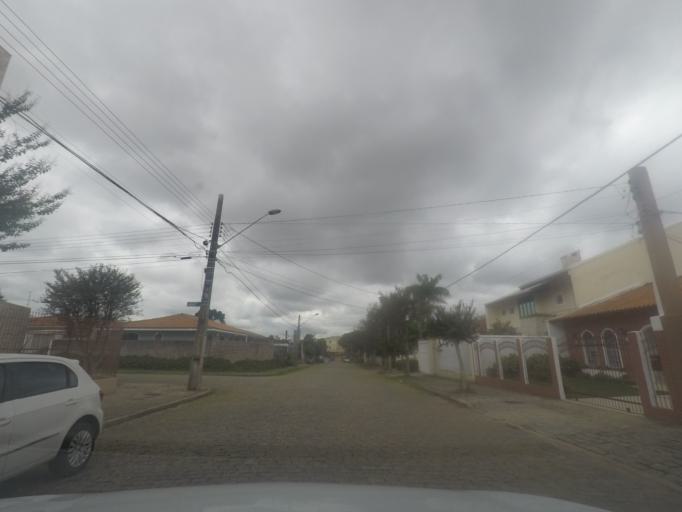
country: BR
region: Parana
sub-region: Curitiba
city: Curitiba
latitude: -25.4402
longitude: -49.2455
